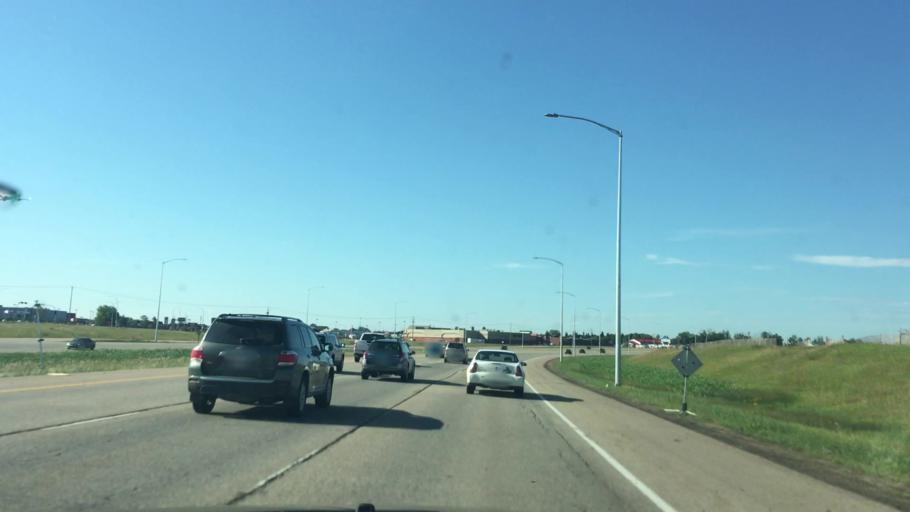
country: CA
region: Alberta
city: Leduc
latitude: 53.2826
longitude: -113.5501
